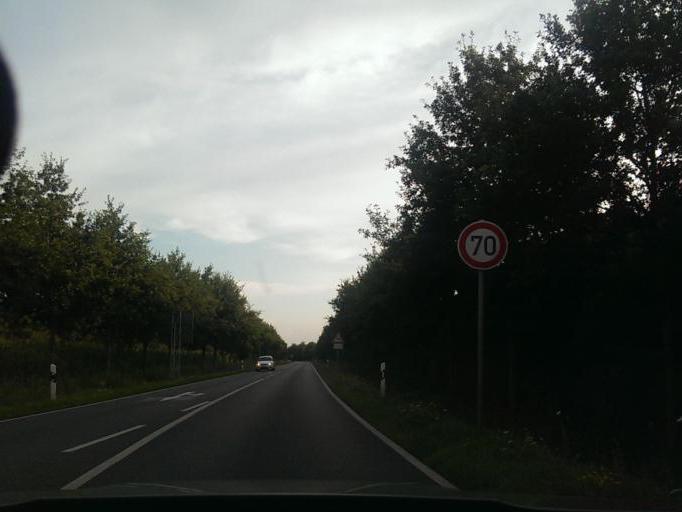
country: DE
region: Lower Saxony
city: Lilienthal
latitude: 53.1563
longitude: 8.9000
